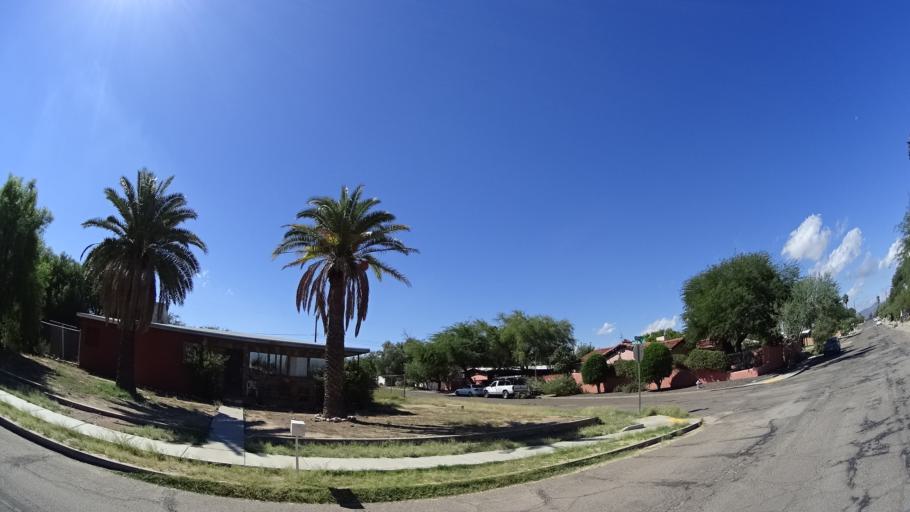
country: US
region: Arizona
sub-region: Pima County
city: Tucson
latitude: 32.2468
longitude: -110.9535
